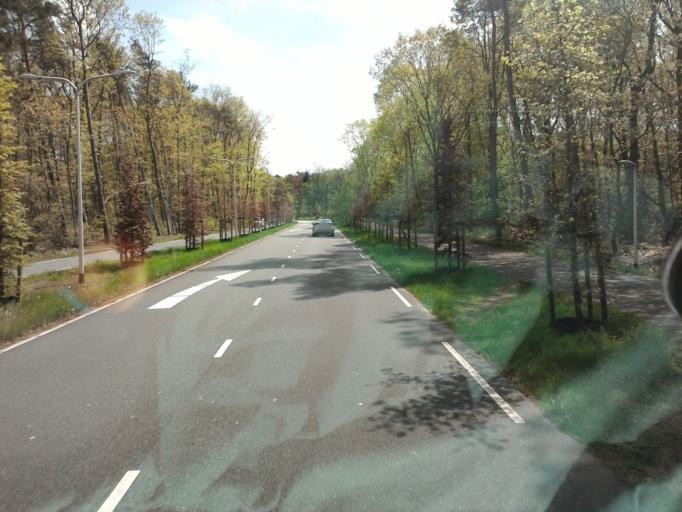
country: NL
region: Utrecht
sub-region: Gemeente Zeist
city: Zeist
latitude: 52.1037
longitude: 5.2633
